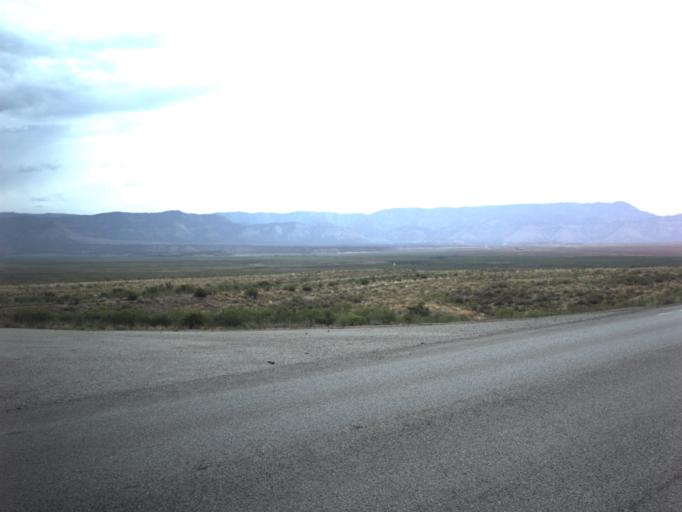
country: US
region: Utah
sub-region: Carbon County
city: Wellington
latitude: 39.5371
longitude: -110.5998
